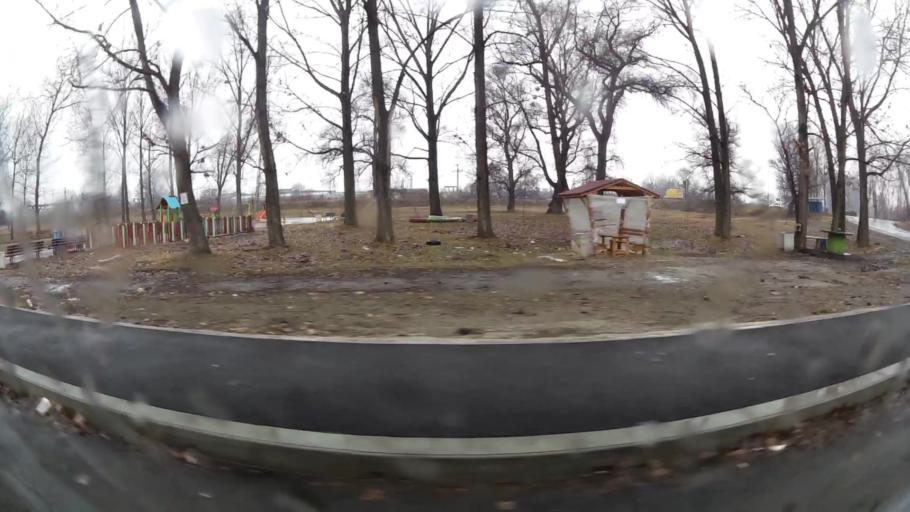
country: BG
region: Sofia-Capital
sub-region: Stolichna Obshtina
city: Sofia
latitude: 42.6646
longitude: 23.4228
